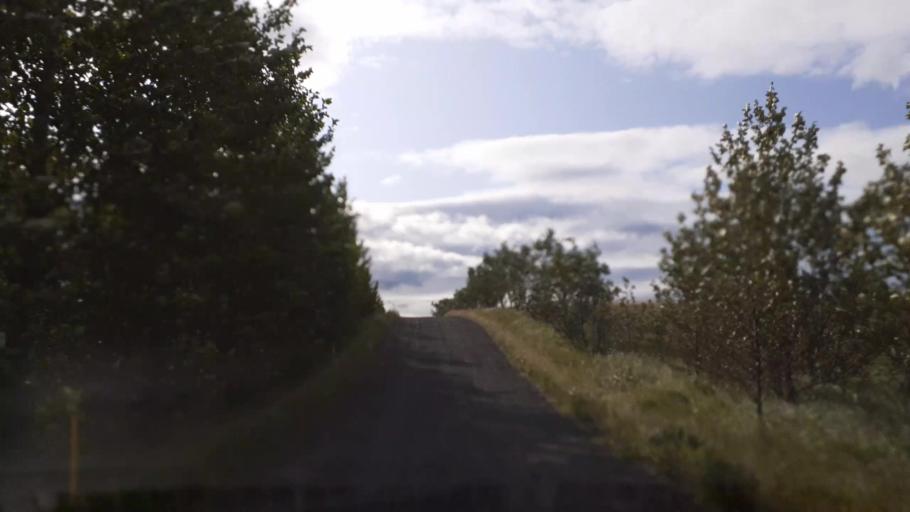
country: IS
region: South
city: Vestmannaeyjar
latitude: 63.7703
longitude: -20.2972
